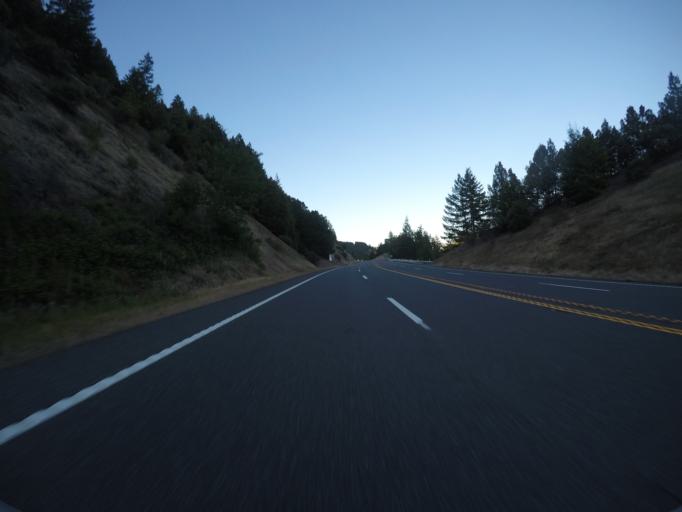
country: US
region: California
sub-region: Mendocino County
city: Laytonville
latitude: 39.8331
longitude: -123.6465
